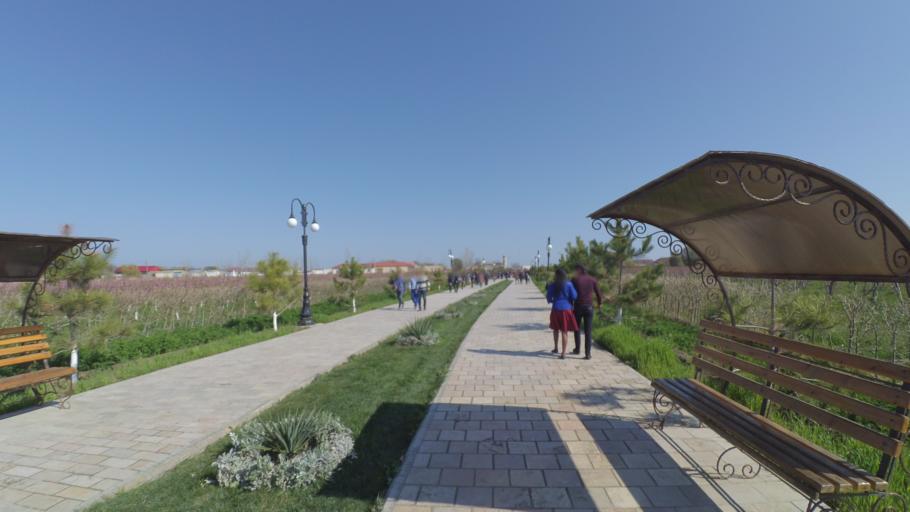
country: UZ
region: Bukhara
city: Kogon
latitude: 39.8031
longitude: 64.5389
